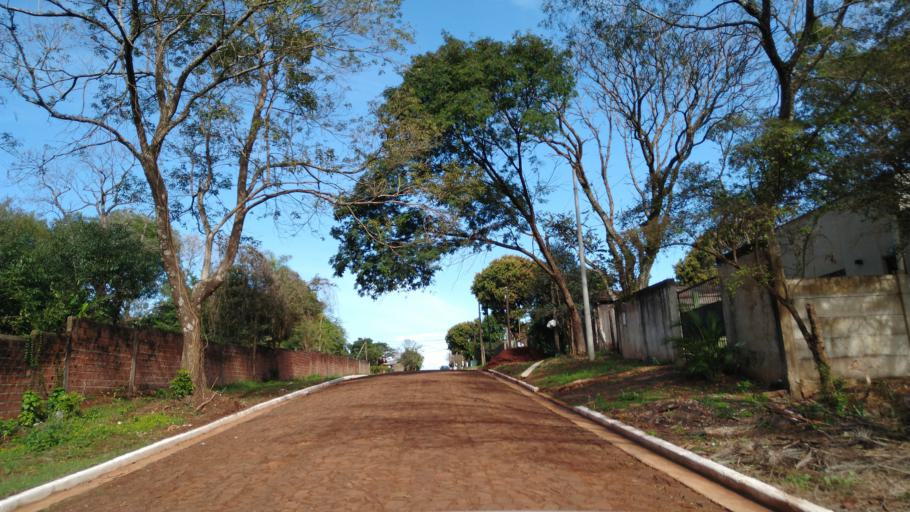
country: AR
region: Misiones
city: Garupa
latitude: -27.4572
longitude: -55.8578
